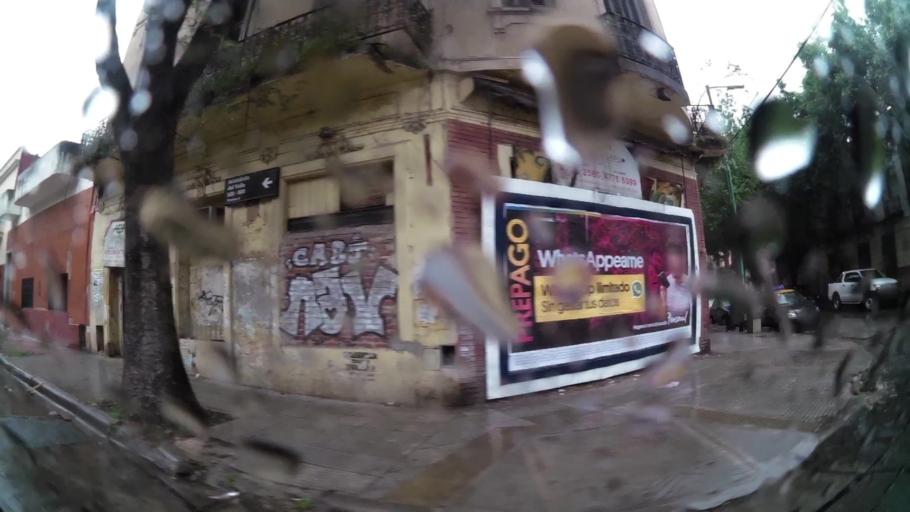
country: AR
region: Buenos Aires F.D.
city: Buenos Aires
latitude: -34.6340
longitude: -58.3632
